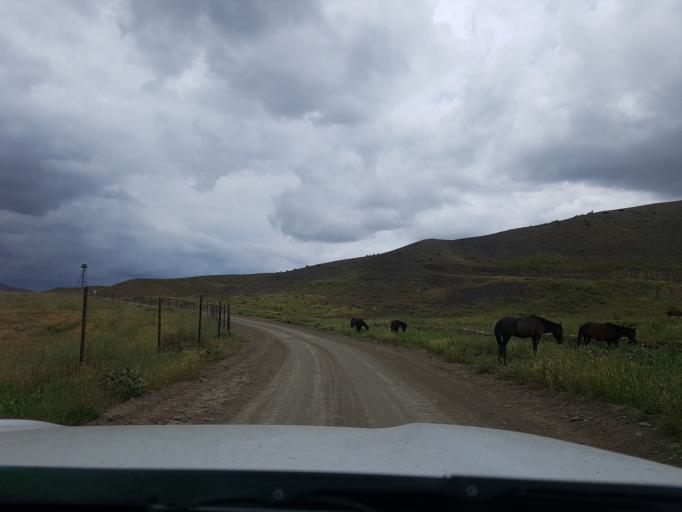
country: TM
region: Ahal
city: Baharly
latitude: 38.2165
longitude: 56.9926
